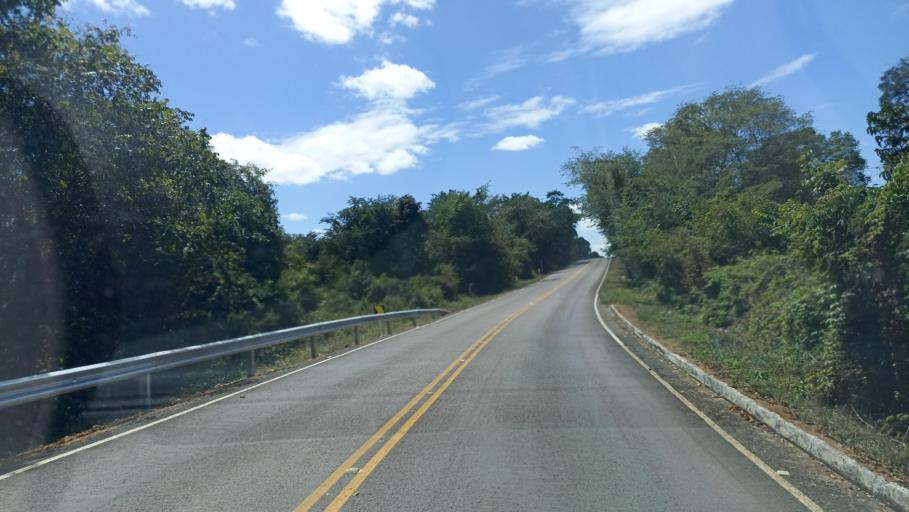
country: BR
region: Bahia
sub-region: Andarai
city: Vera Cruz
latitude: -12.7517
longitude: -41.3285
